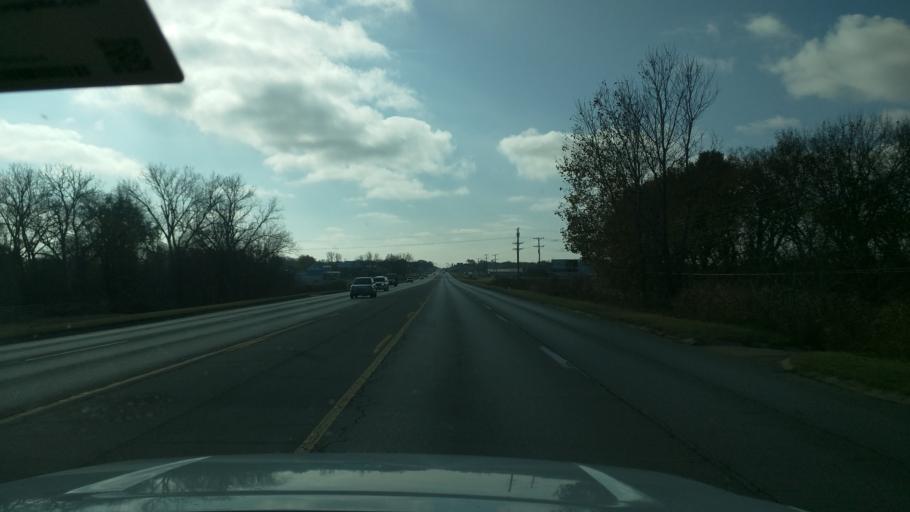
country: US
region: Oklahoma
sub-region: Washington County
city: Dewey
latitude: 36.7803
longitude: -95.9355
